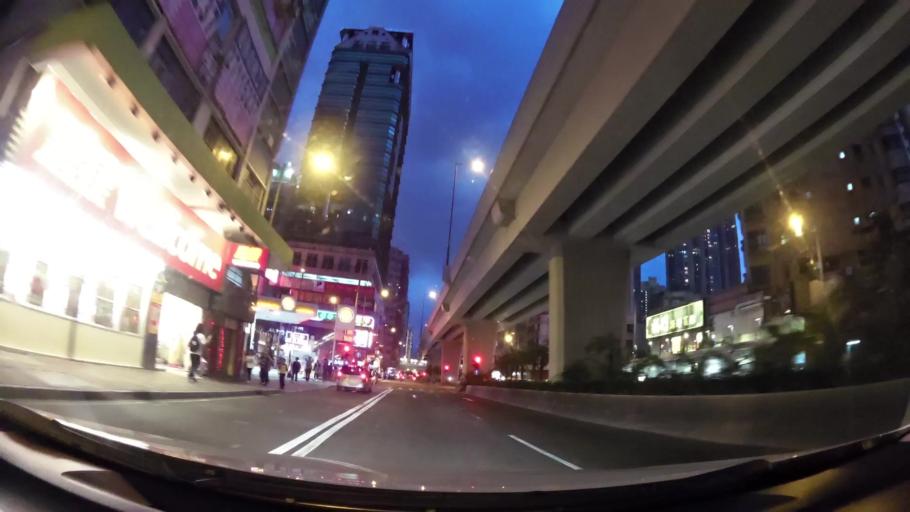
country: HK
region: Sham Shui Po
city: Sham Shui Po
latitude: 22.3209
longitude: 114.1659
